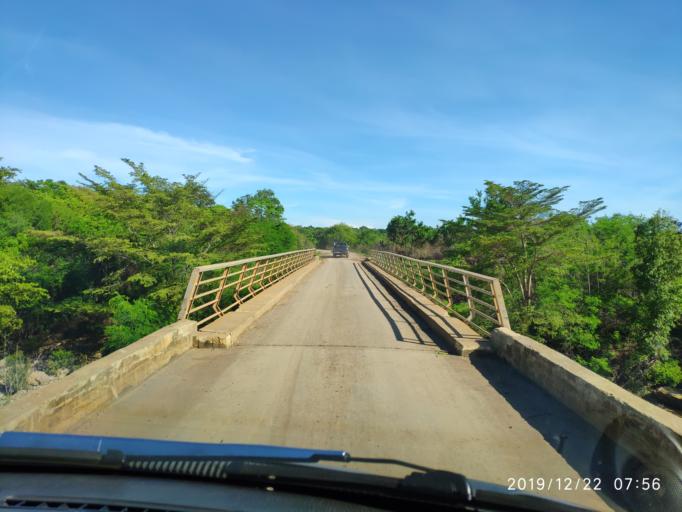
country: MG
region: Diana
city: Ambilobe
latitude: -12.9594
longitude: 49.1445
